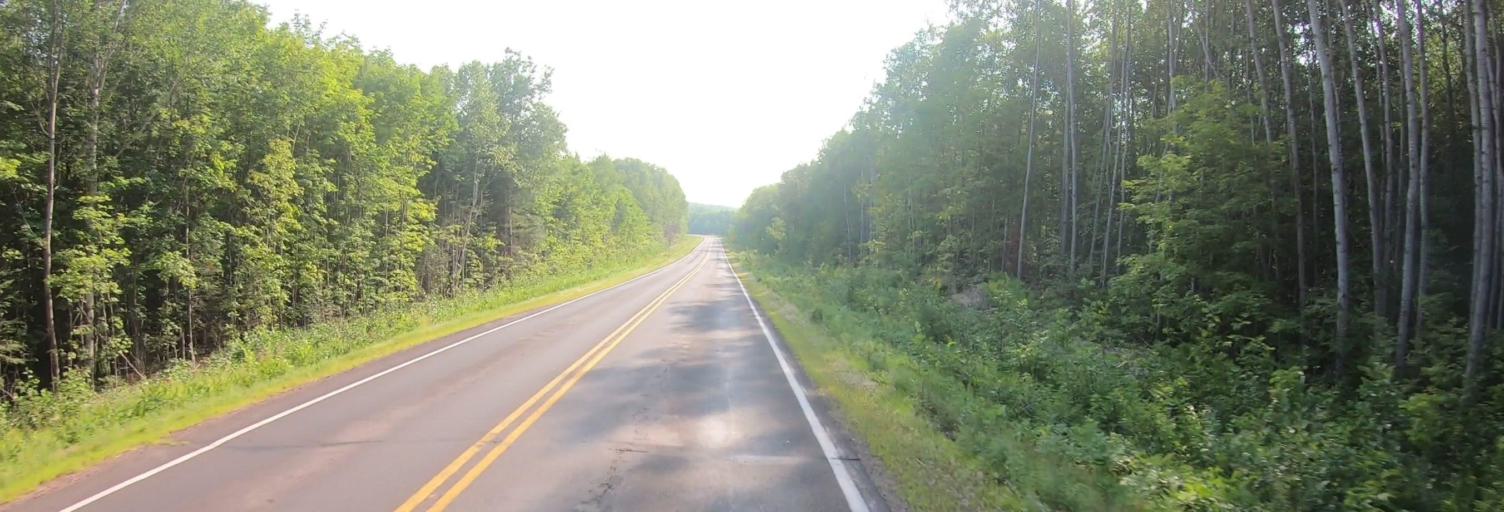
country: US
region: Wisconsin
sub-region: Ashland County
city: Ashland
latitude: 46.2941
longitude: -90.8157
